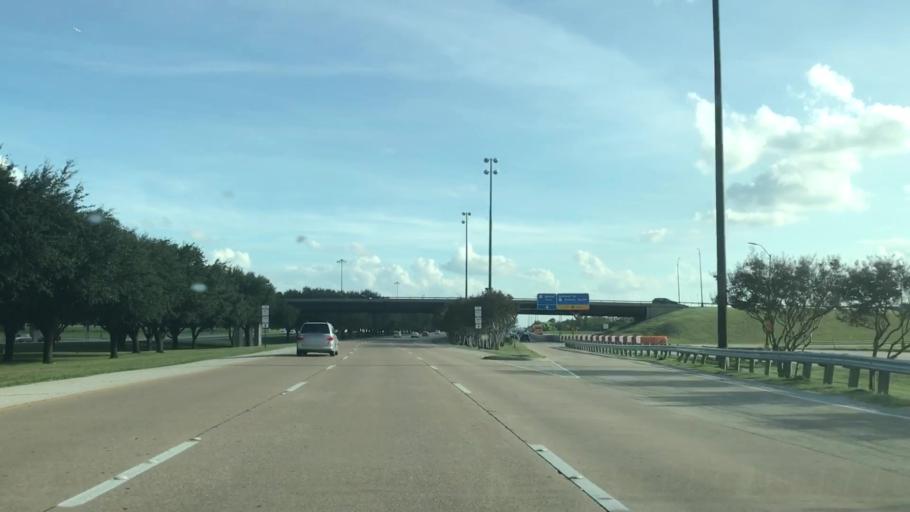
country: US
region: Texas
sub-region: Tarrant County
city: Euless
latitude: 32.8636
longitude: -97.0411
